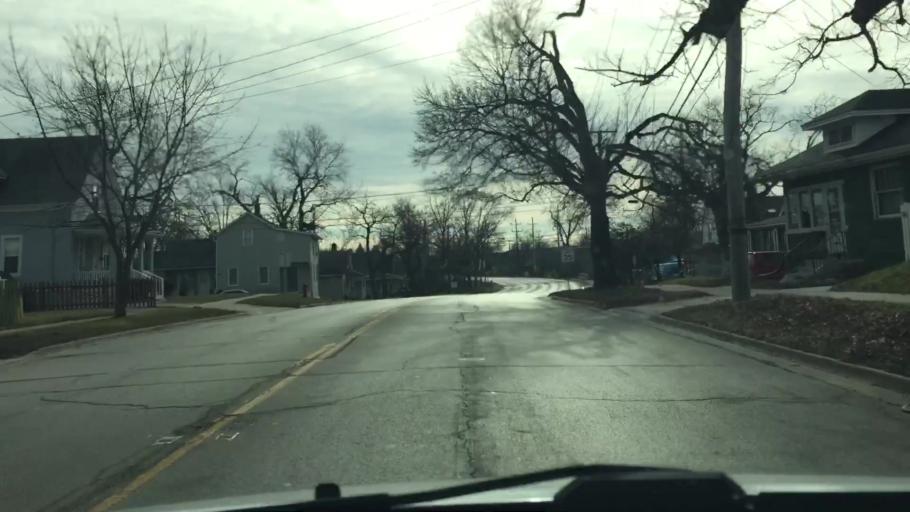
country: US
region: Illinois
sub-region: Kane County
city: Elgin
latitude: 42.0159
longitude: -88.2688
